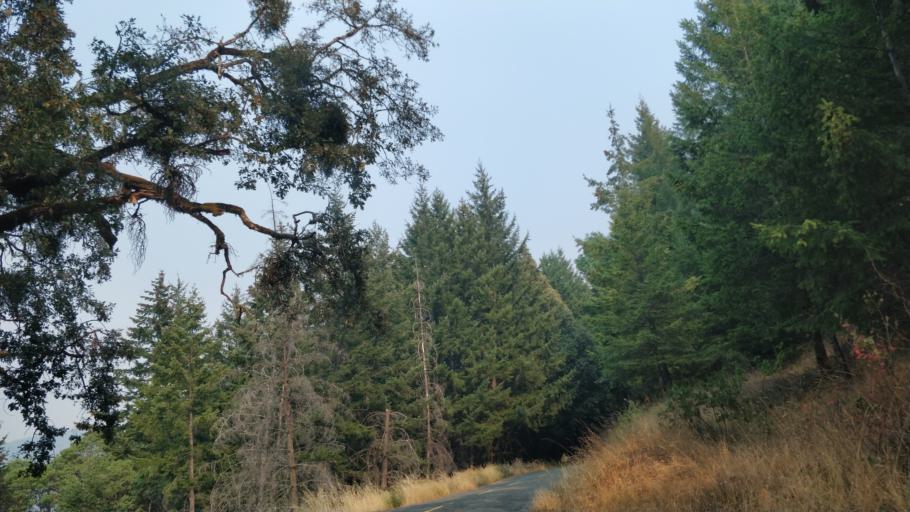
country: US
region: California
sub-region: Humboldt County
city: Rio Dell
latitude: 40.2636
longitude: -124.1108
